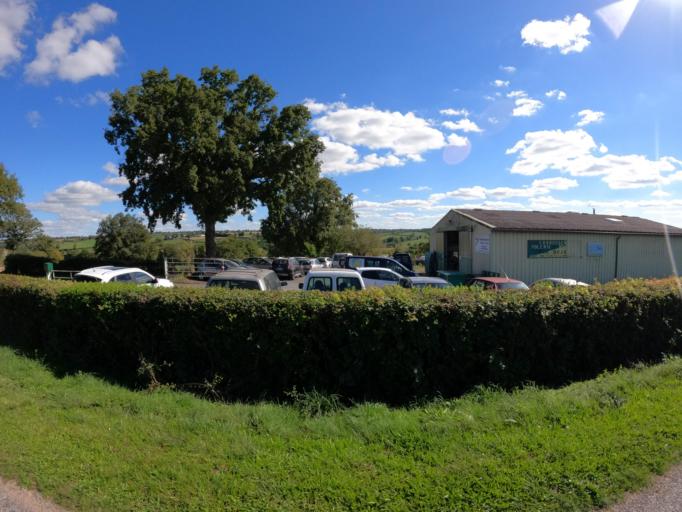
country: FR
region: Auvergne
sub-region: Departement de l'Allier
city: Buxieres-les-Mines
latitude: 46.3983
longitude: 2.8891
